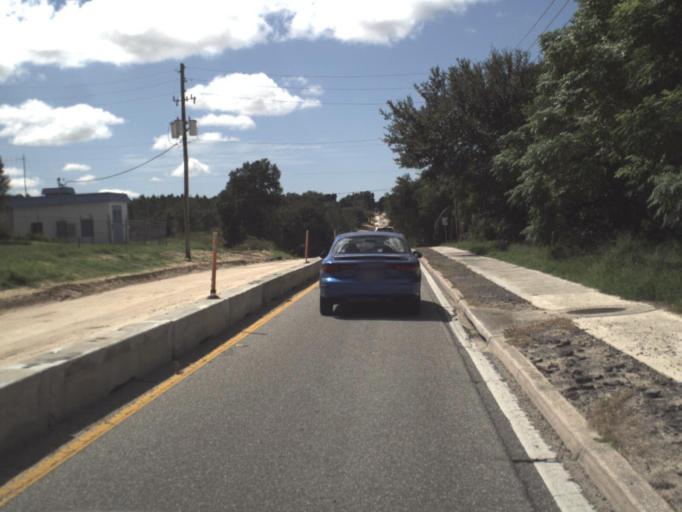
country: US
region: Florida
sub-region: Polk County
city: Haines City
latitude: 28.0948
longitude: -81.6233
